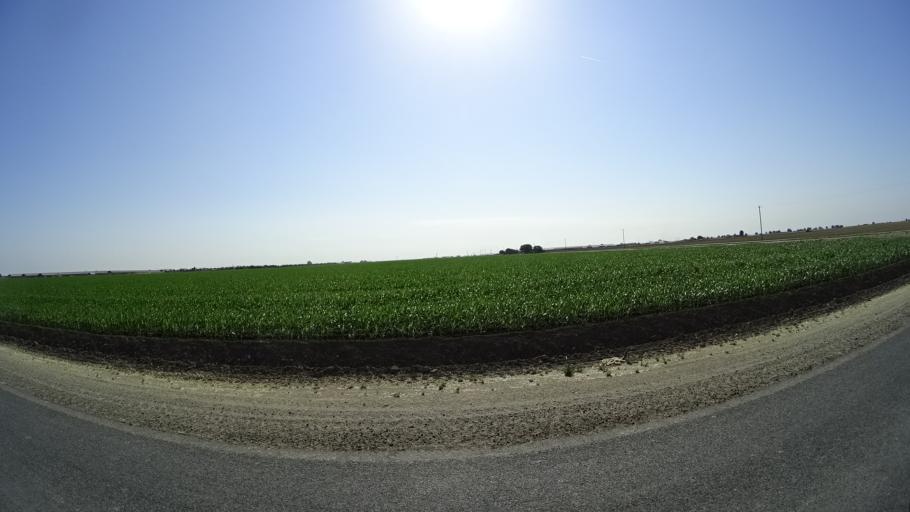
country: US
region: California
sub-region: Kings County
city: Home Garden
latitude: 36.2413
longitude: -119.5831
